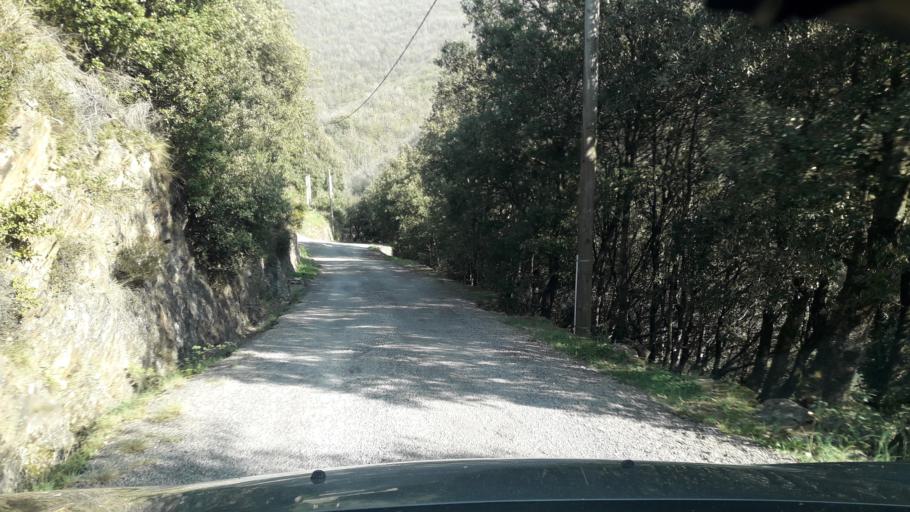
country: FR
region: Languedoc-Roussillon
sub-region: Departement du Gard
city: Valleraugue
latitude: 44.1092
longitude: 3.6915
